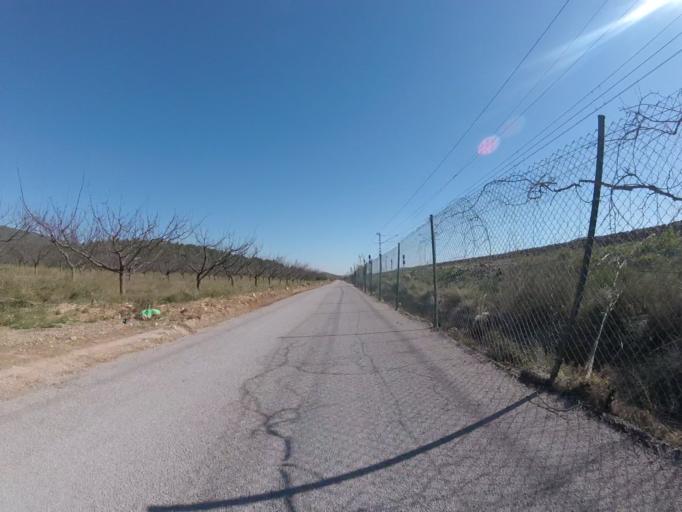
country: ES
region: Valencia
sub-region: Provincia de Castello
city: Santa Magdalena de Pulpis
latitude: 40.3427
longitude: 0.2655
